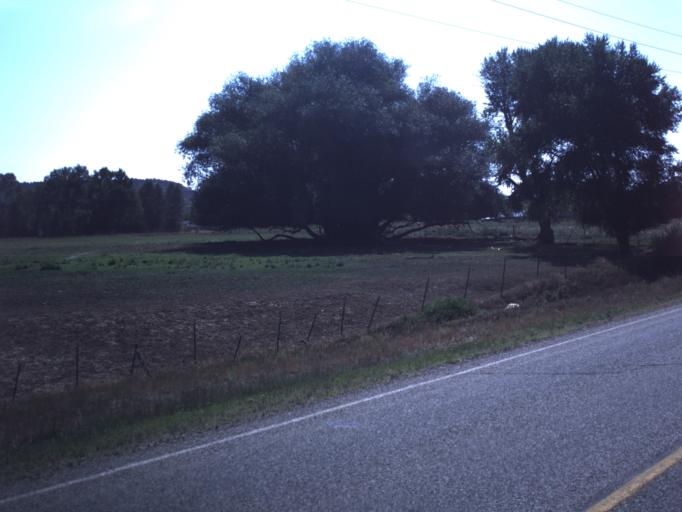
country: US
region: Utah
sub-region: Duchesne County
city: Duchesne
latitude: 40.3574
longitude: -110.7160
